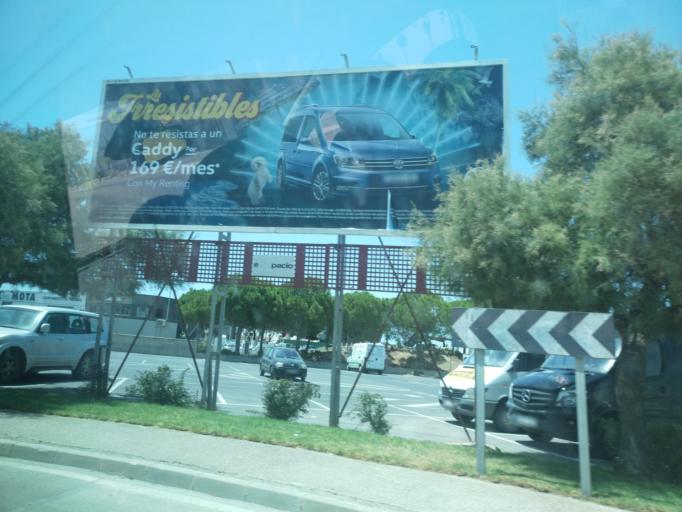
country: ES
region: Andalusia
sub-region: Provincia de Cadiz
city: Chiclana de la Frontera
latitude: 36.4294
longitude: -6.1508
